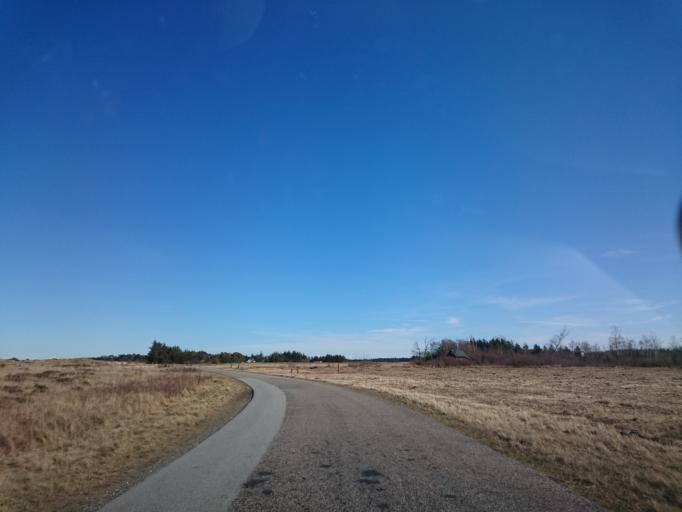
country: DK
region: North Denmark
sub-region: Frederikshavn Kommune
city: Strandby
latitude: 57.6246
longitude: 10.3434
